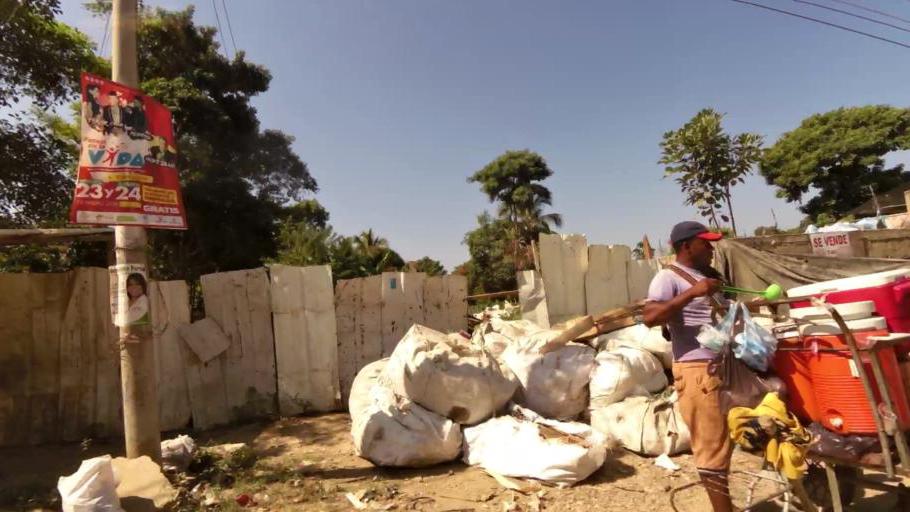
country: CO
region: Bolivar
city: Cartagena
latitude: 10.3666
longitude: -75.4916
